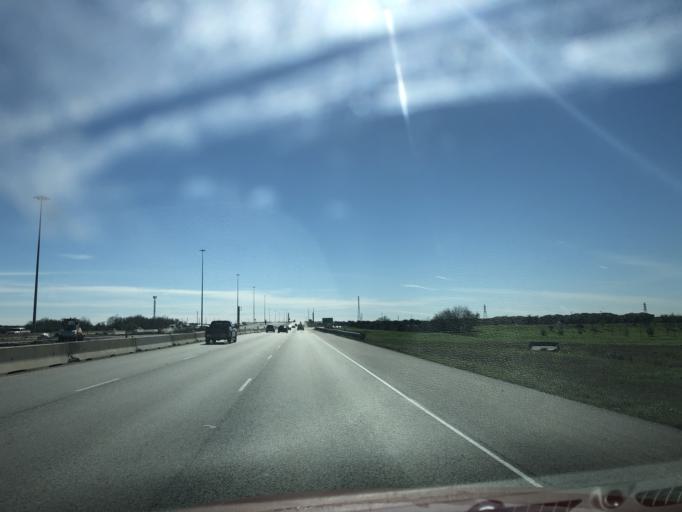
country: US
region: Texas
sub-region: Brazoria County
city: Brookside Village
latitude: 29.6339
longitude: -95.3874
